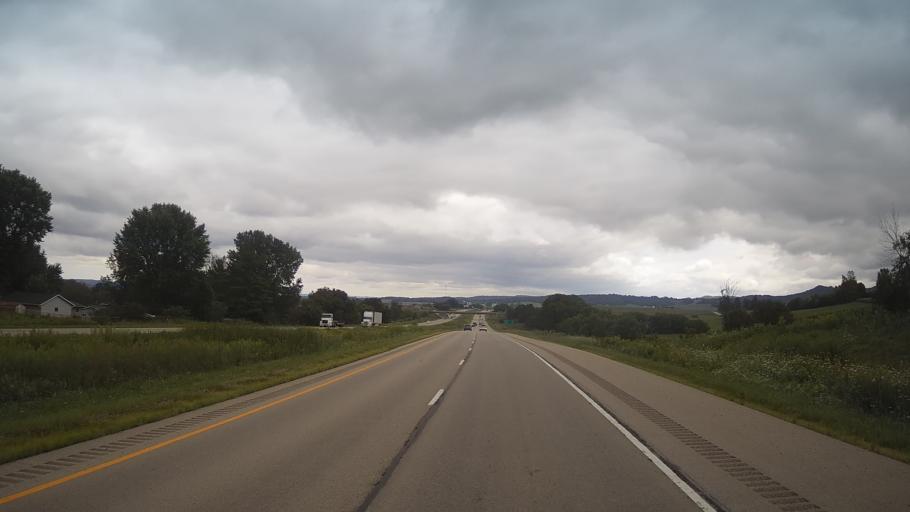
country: US
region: Wisconsin
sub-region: La Crosse County
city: Bangor
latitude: 43.8859
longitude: -90.9893
